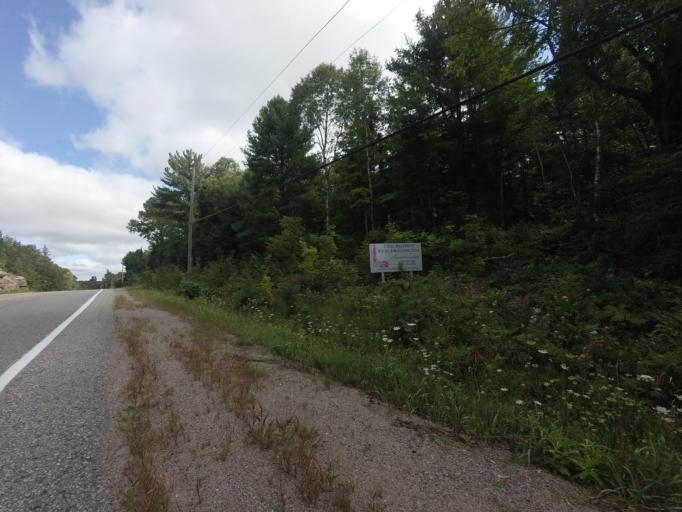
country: CA
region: Ontario
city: Omemee
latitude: 44.7935
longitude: -78.6398
